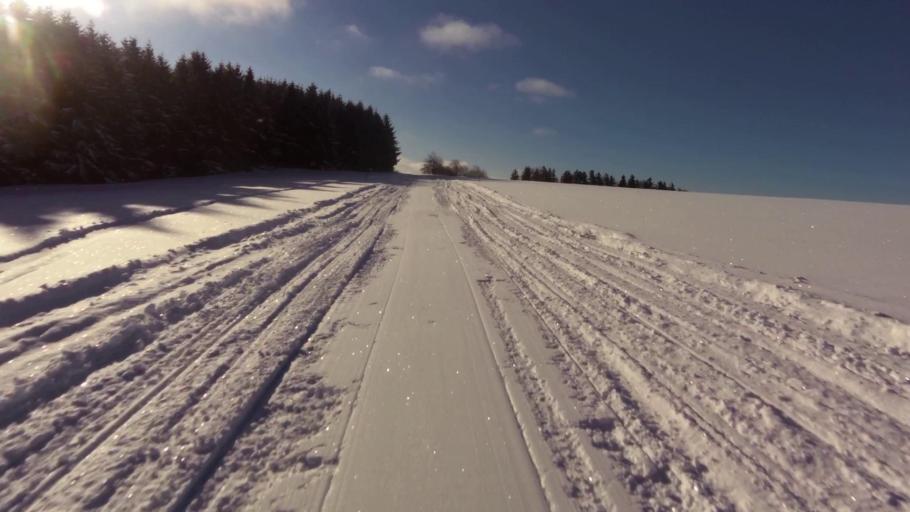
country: US
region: New York
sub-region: Chautauqua County
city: Falconer
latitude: 42.2665
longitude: -79.1857
